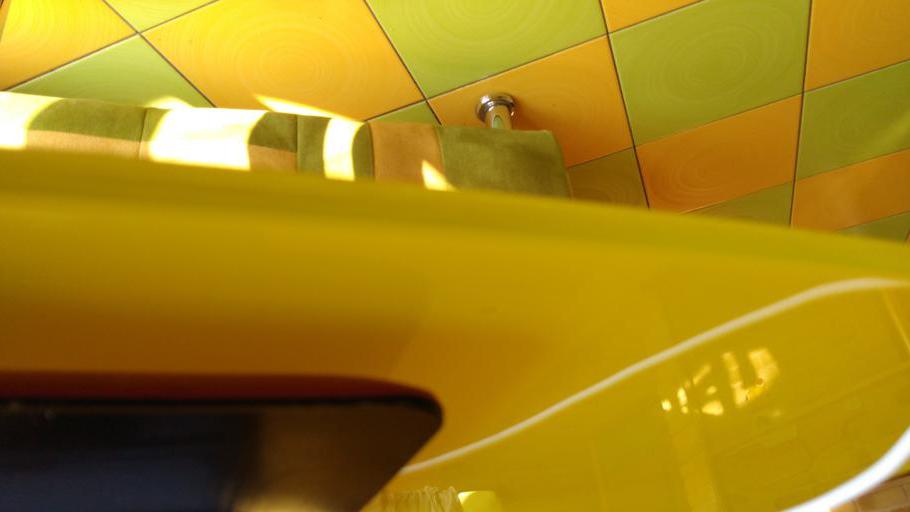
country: RU
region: Tverskaya
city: Krasnomayskiy
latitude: 57.6031
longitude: 34.2389
